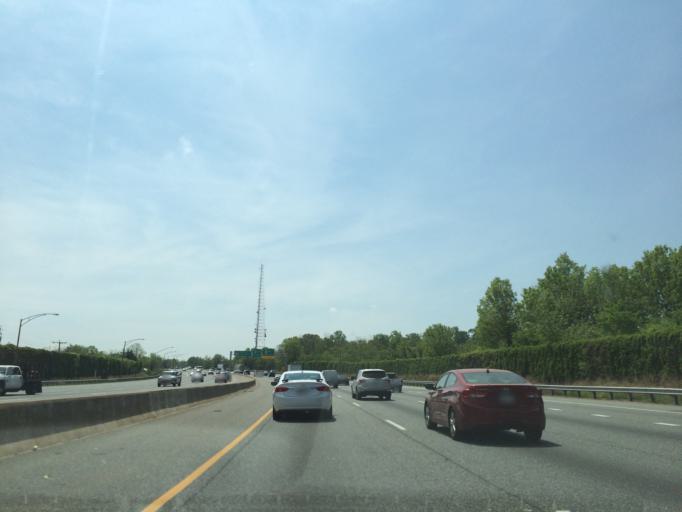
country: US
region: Maryland
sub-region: Baltimore County
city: Catonsville
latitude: 39.2911
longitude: -76.7421
